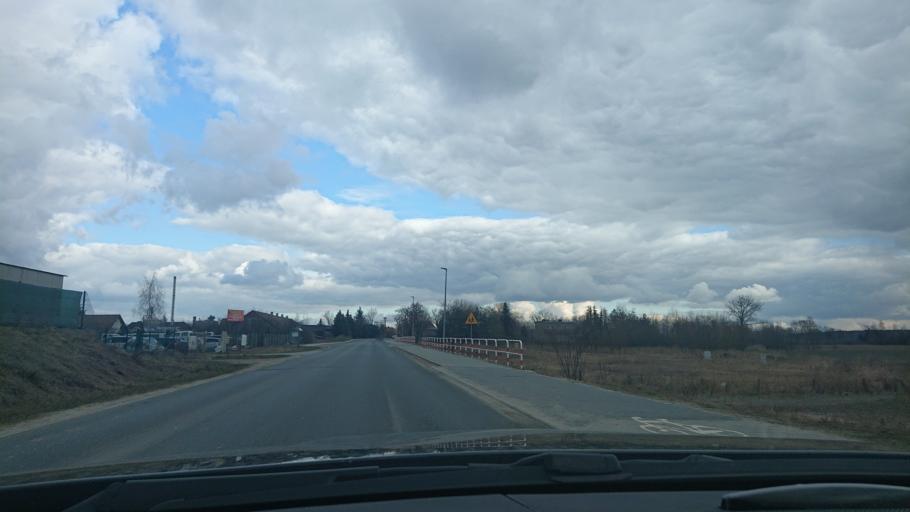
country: PL
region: Greater Poland Voivodeship
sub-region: Powiat gnieznienski
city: Gniezno
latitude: 52.5441
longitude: 17.6589
